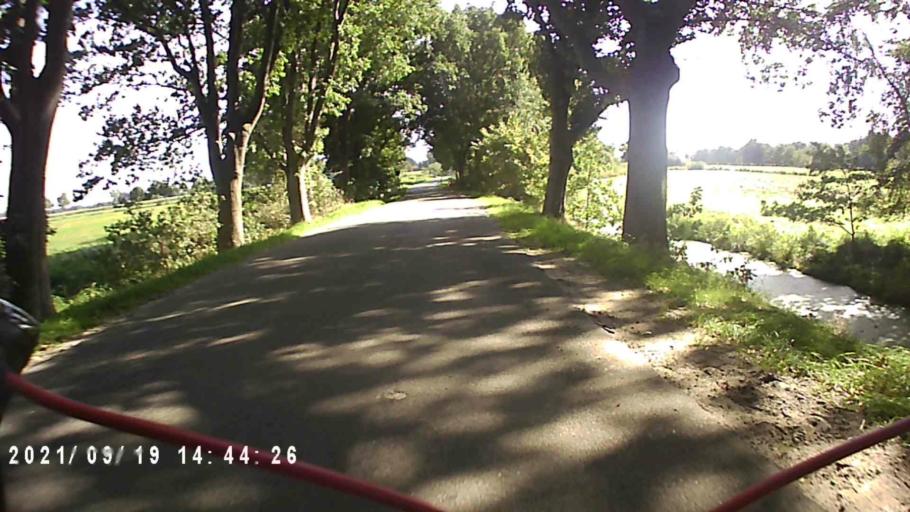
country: DE
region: Lower Saxony
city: Bunde
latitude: 53.1267
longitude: 7.1813
